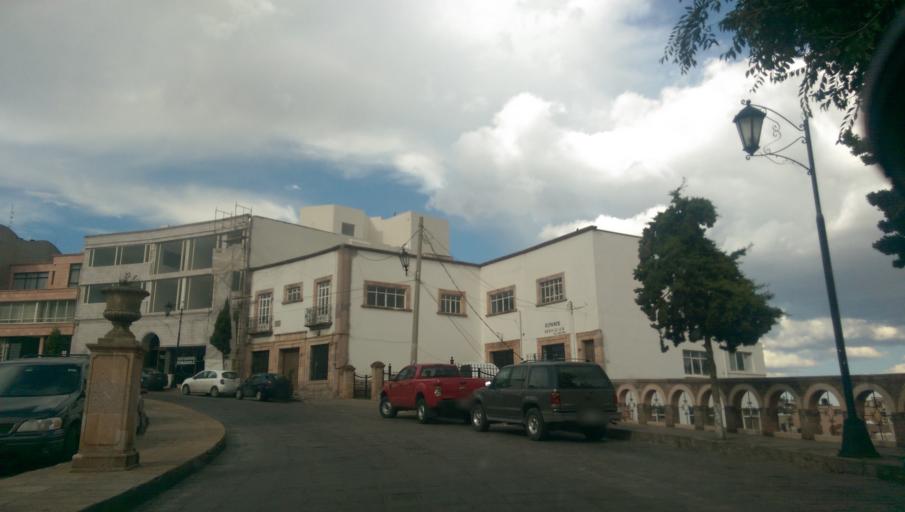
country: MX
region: Zacatecas
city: Zacatecas
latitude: 22.7692
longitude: -102.5759
